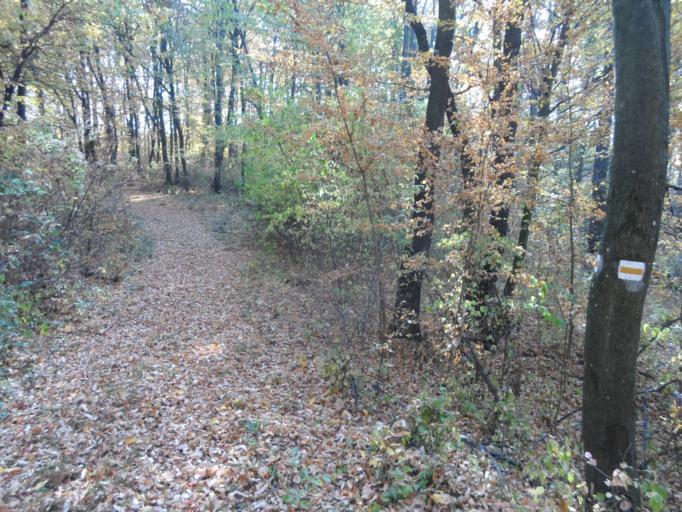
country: HU
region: Veszprem
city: Ajka
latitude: 47.2111
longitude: 17.6145
